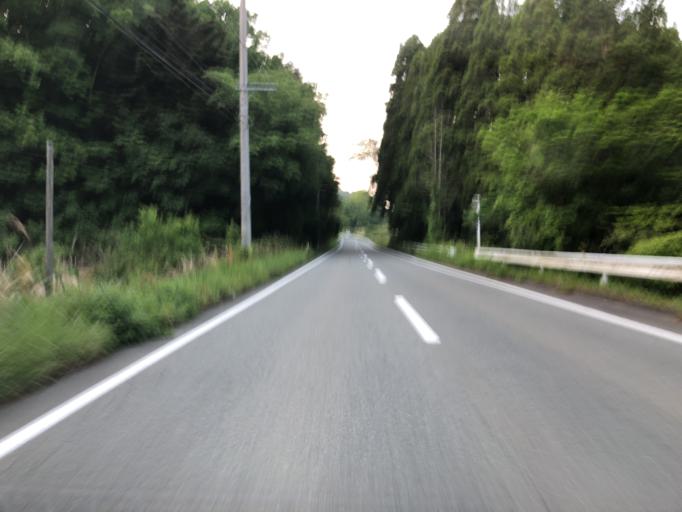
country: JP
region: Fukushima
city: Namie
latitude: 37.2627
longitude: 140.9735
